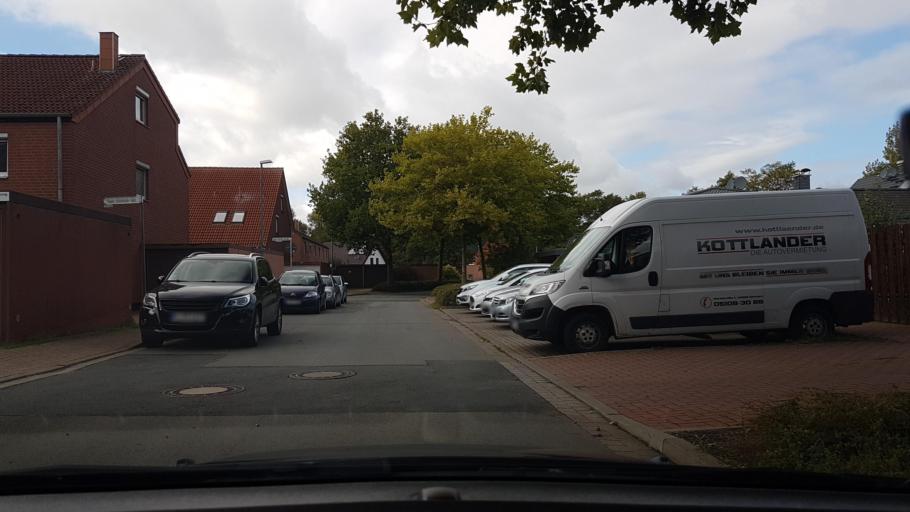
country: DE
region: Lower Saxony
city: Ronnenberg
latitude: 52.3418
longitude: 9.6734
